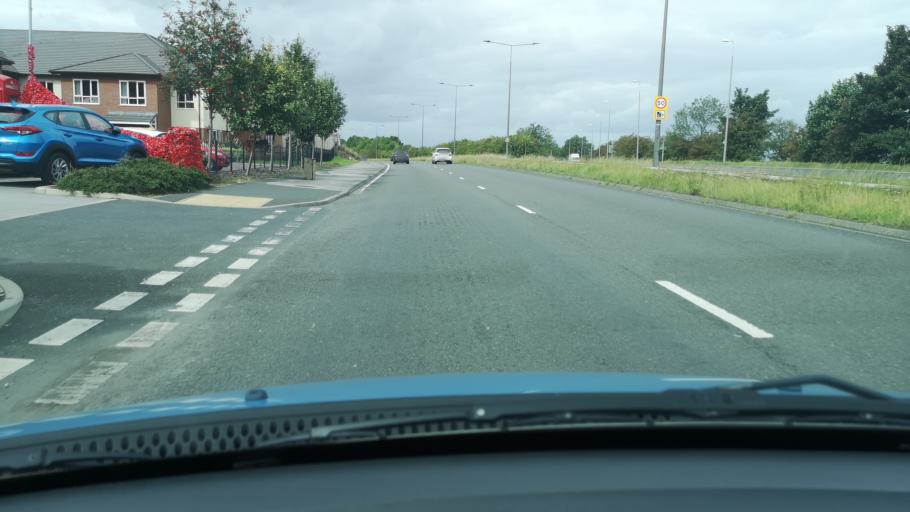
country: GB
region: England
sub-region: Doncaster
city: Carcroft
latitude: 53.5737
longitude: -1.2029
